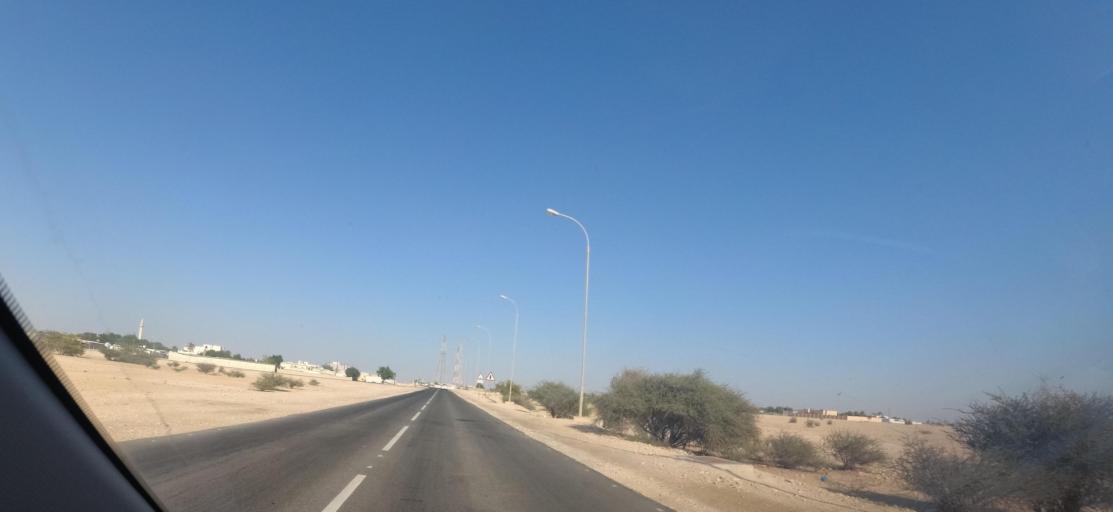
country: QA
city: Al Ghuwayriyah
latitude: 25.8249
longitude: 51.2438
